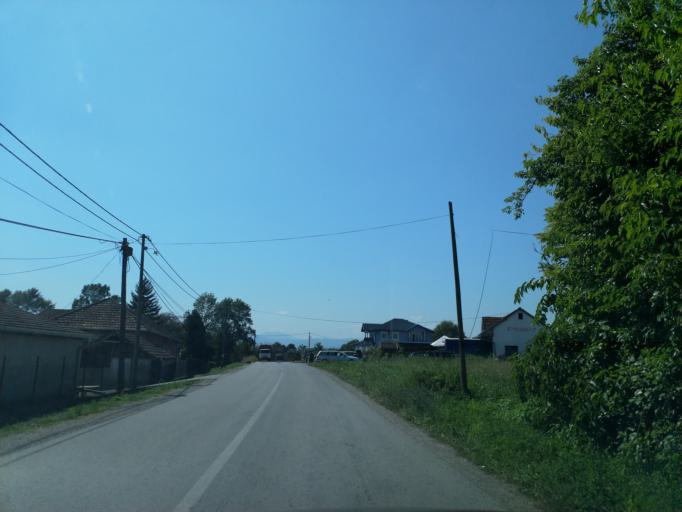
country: RS
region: Central Serbia
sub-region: Rasinski Okrug
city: Trstenik
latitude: 43.6267
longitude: 21.1397
